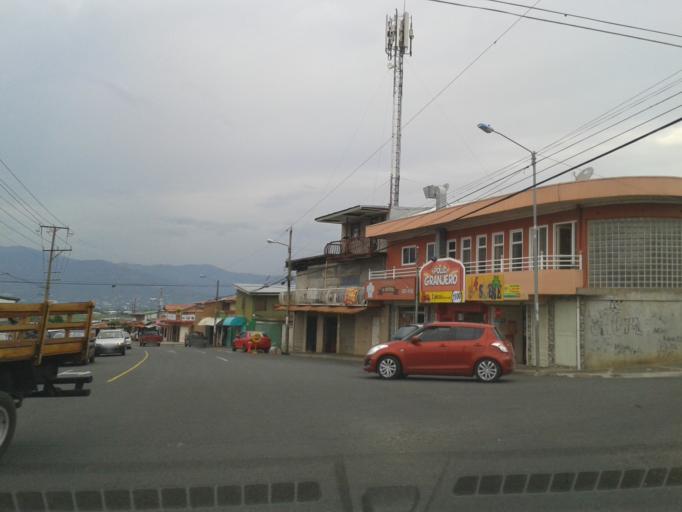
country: CR
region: Heredia
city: San Francisco
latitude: 9.9819
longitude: -84.1185
